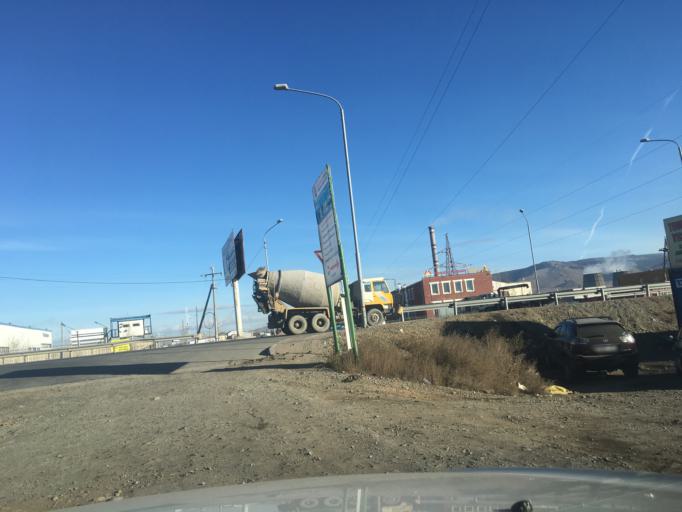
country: MN
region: Ulaanbaatar
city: Ulaanbaatar
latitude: 47.9013
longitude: 106.7852
